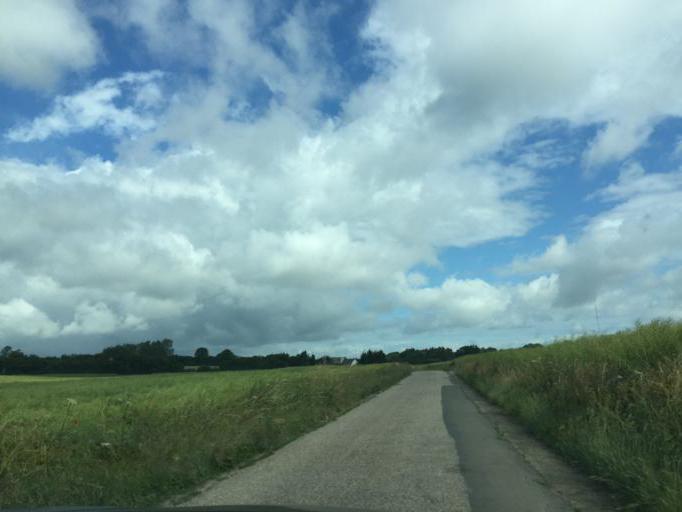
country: DK
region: South Denmark
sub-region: Faaborg-Midtfyn Kommune
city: Ringe
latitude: 55.2623
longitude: 10.4773
